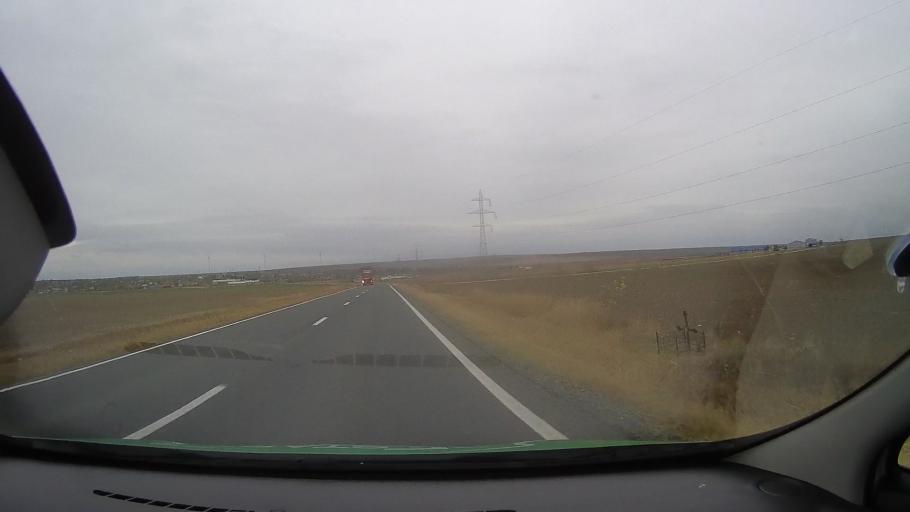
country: RO
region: Constanta
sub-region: Comuna Nicolae Balcescu
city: Dorobantu
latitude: 44.4172
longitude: 28.3148
